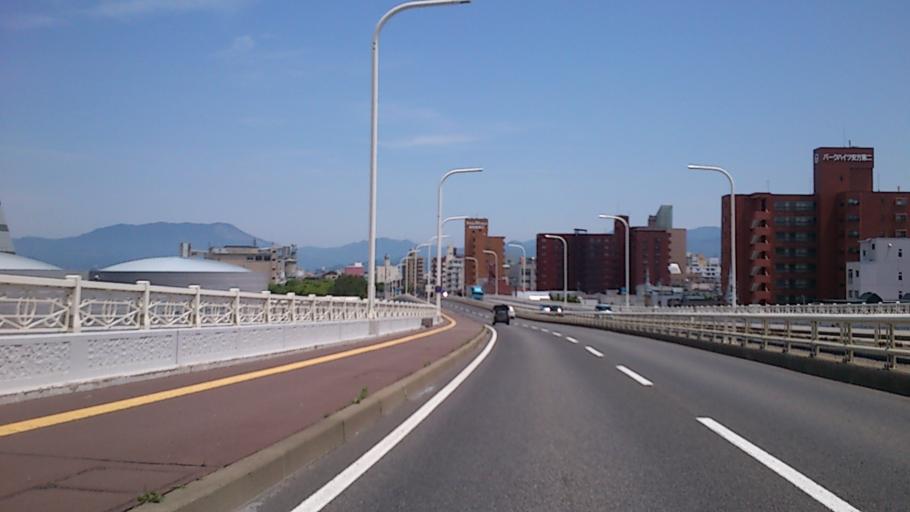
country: JP
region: Aomori
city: Aomori Shi
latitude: 40.8294
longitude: 140.7395
